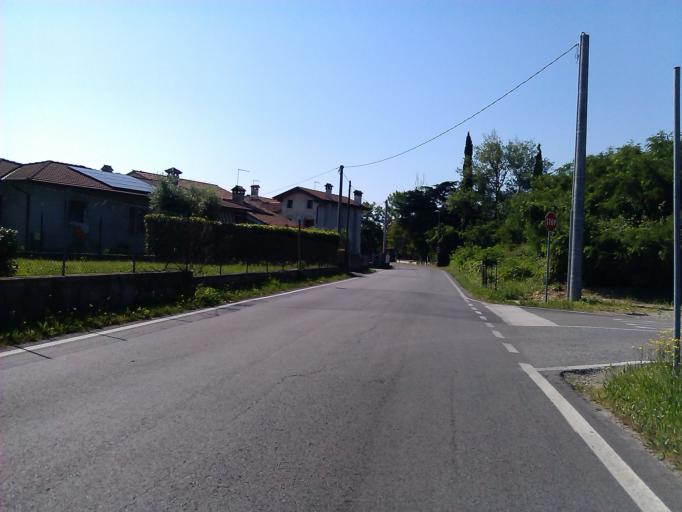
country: IT
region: Veneto
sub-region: Provincia di Vicenza
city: San Zeno-San Giuseppe
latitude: 45.7574
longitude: 11.7684
